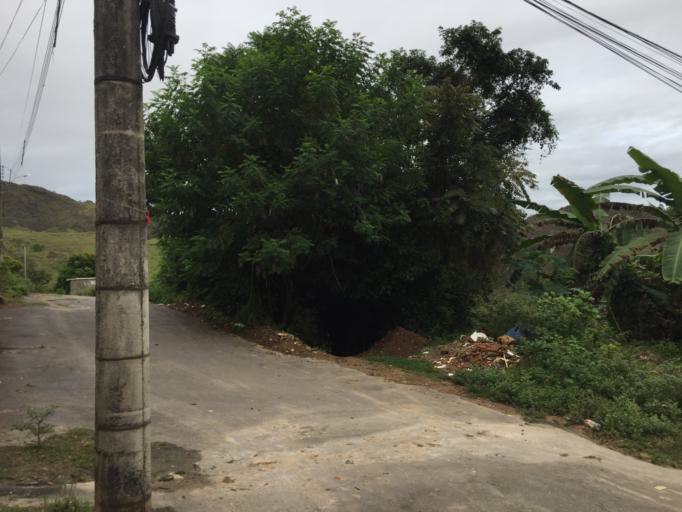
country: BR
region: Minas Gerais
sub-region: Sao Joao Del Rei
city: Sao Joao del Rei
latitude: -21.1271
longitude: -44.2666
